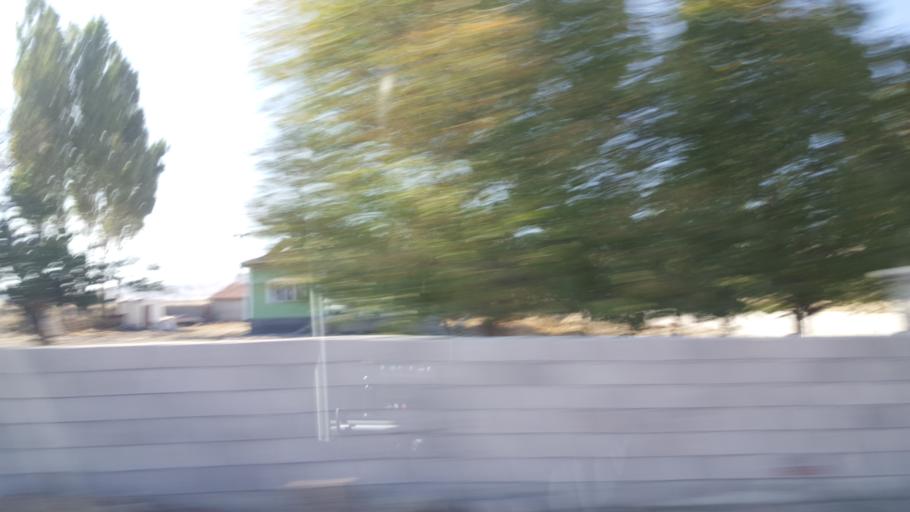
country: TR
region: Ankara
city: Altpinar
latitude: 39.2676
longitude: 32.7540
